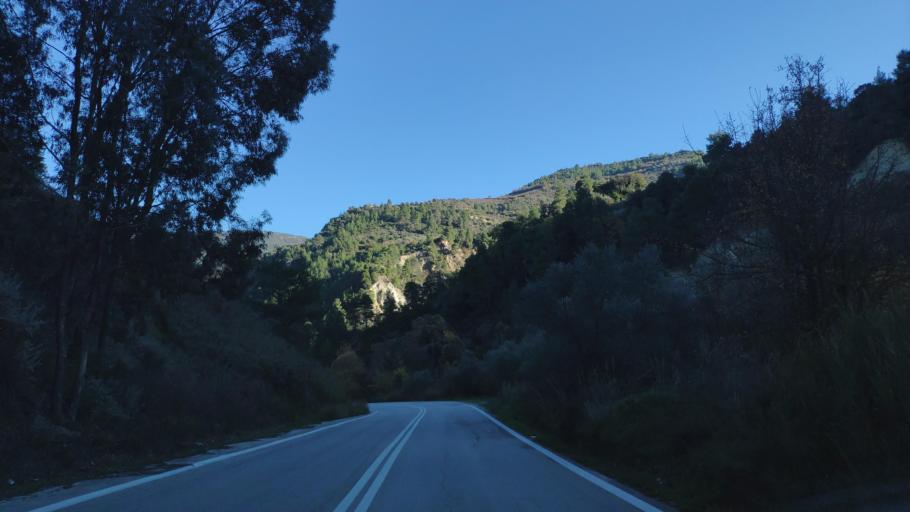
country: GR
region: Peloponnese
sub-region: Nomos Korinthias
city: Xylokastro
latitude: 38.0090
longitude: 22.5304
